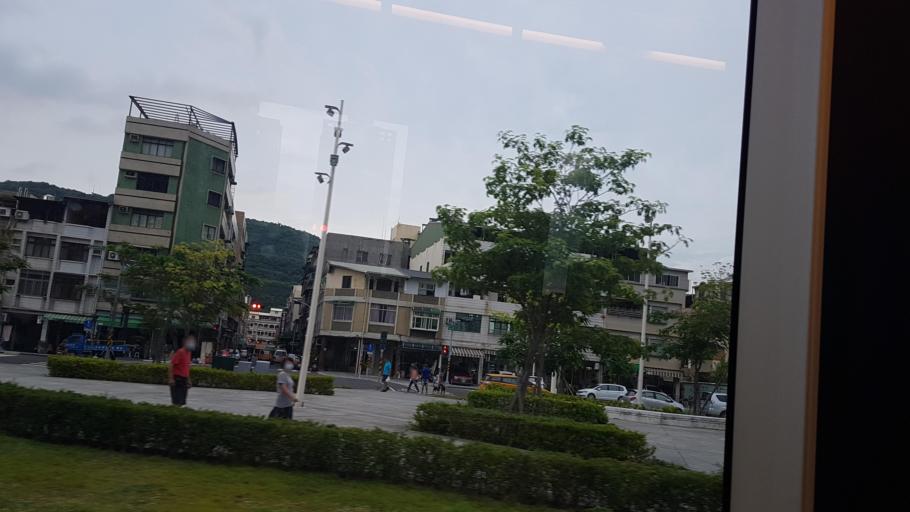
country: TW
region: Kaohsiung
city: Kaohsiung
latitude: 22.6499
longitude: 120.2816
